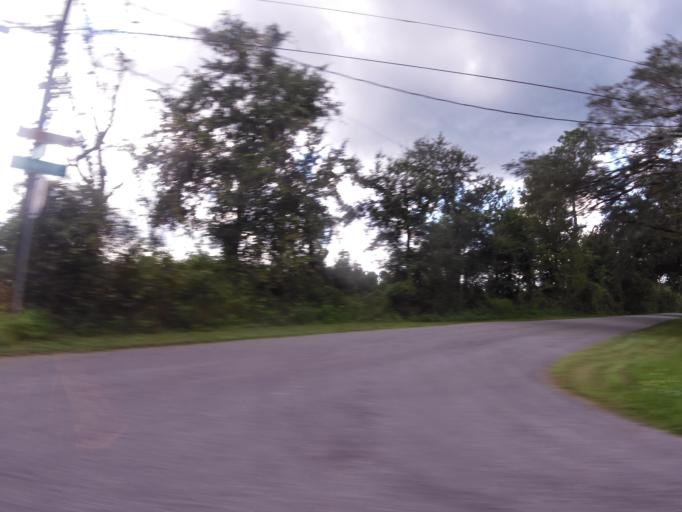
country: US
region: Florida
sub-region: Putnam County
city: East Palatka
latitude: 29.7693
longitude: -81.4781
